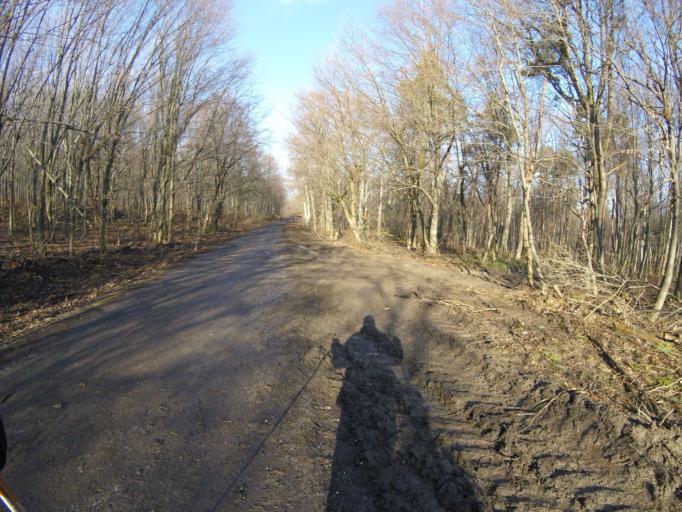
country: HU
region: Komarom-Esztergom
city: Pilismarot
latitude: 47.7464
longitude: 18.8828
